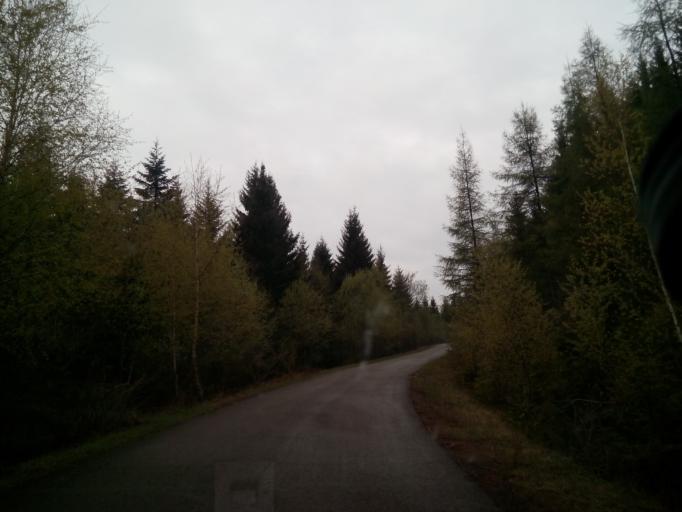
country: SK
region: Zilinsky
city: Oravska Lesna
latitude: 49.3074
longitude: 19.1964
